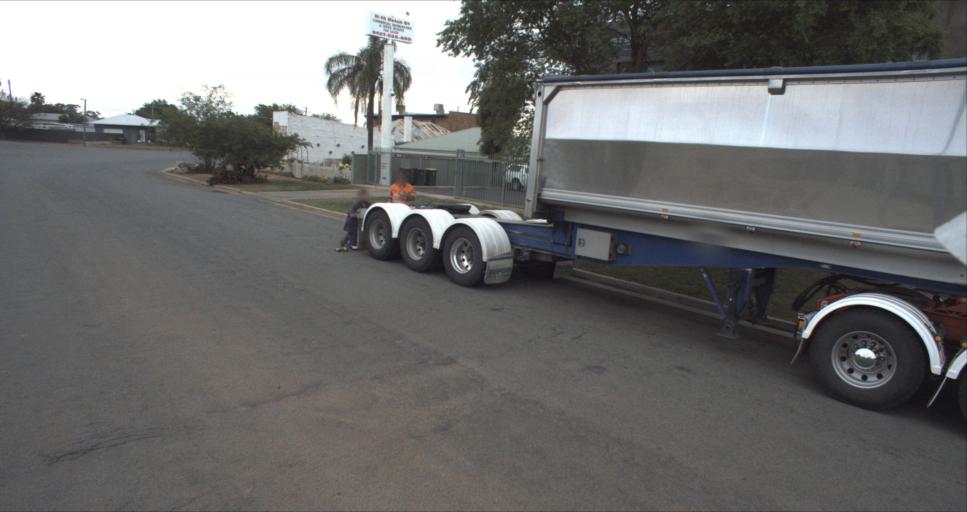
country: AU
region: New South Wales
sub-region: Leeton
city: Leeton
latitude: -34.5530
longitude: 146.4008
